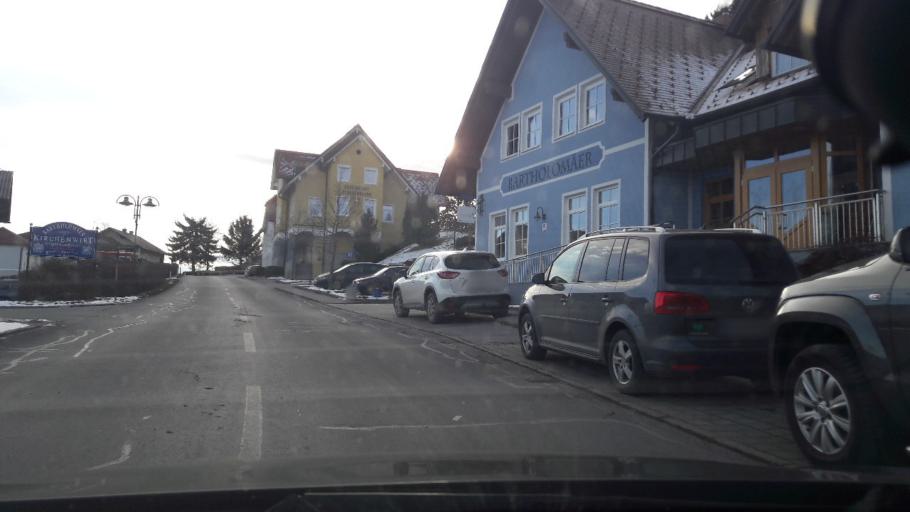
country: AT
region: Styria
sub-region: Politischer Bezirk Graz-Umgebung
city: Sankt Bartholoma
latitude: 47.0701
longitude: 15.2578
